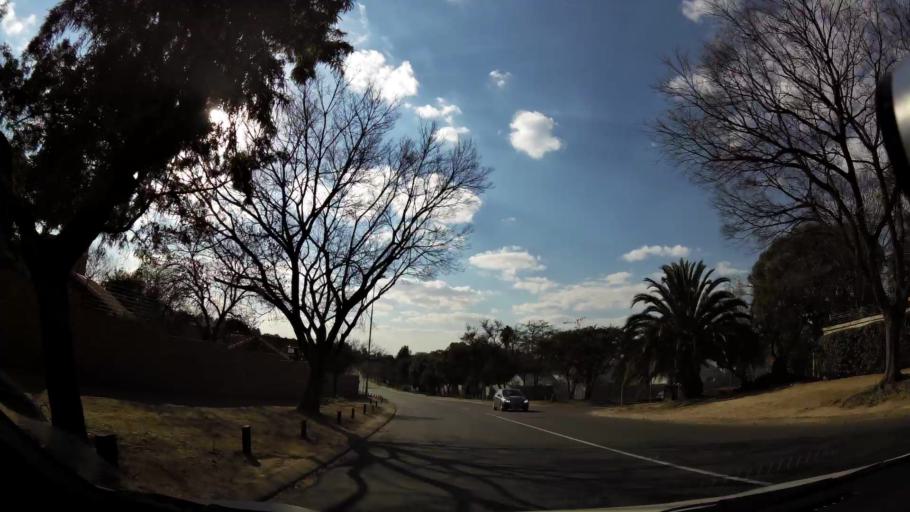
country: ZA
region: Gauteng
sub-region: City of Johannesburg Metropolitan Municipality
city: Diepsloot
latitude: -26.0146
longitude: 28.0318
